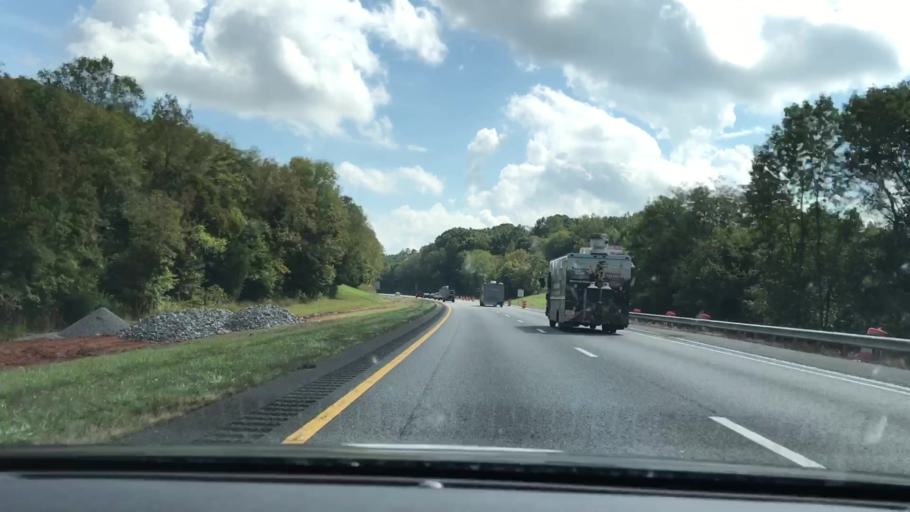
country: US
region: Tennessee
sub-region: Montgomery County
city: Clarksville
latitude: 36.5391
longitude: -87.2387
